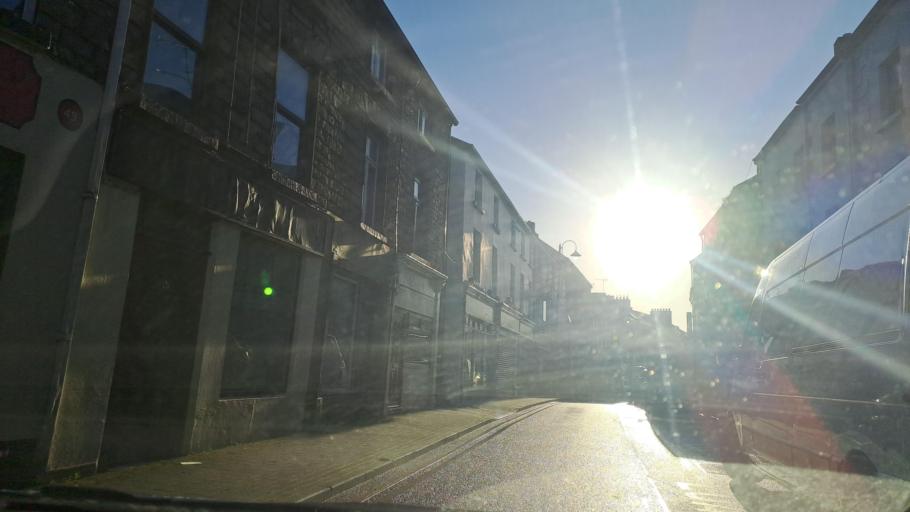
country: IE
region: Ulster
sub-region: County Monaghan
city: Monaghan
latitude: 54.2479
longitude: -6.9669
